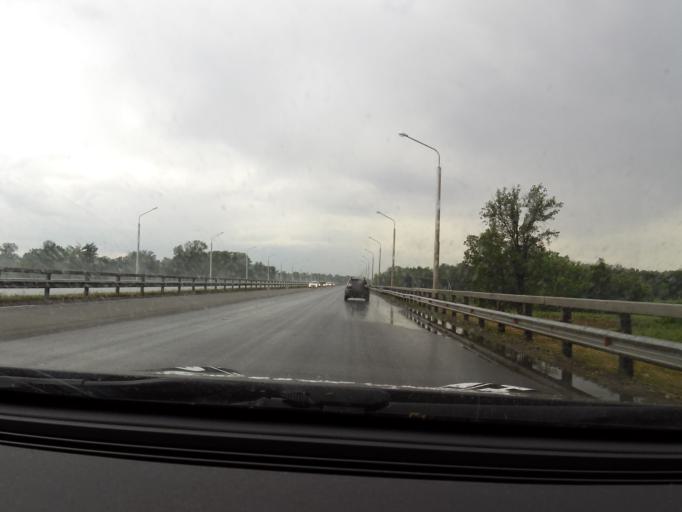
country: RU
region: Bashkortostan
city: Mikhaylovka
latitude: 54.7795
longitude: 55.9295
